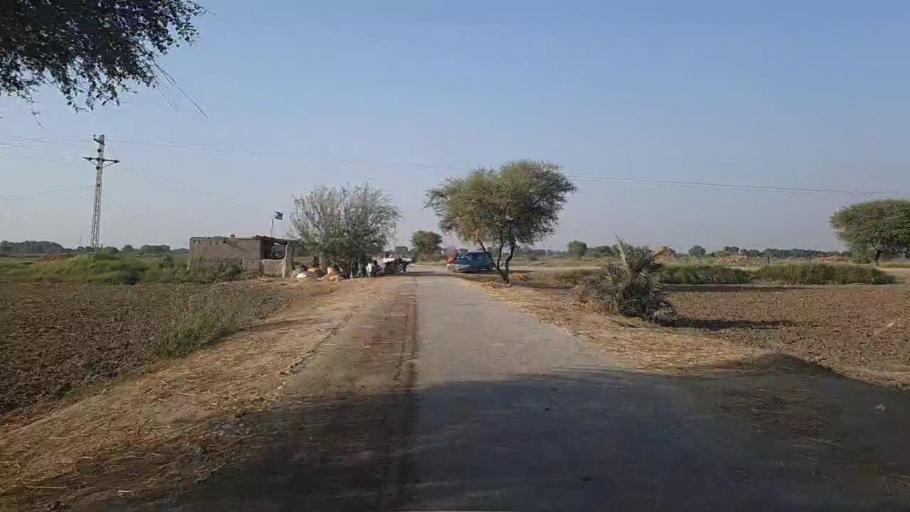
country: PK
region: Sindh
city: Kashmor
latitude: 28.4171
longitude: 69.4101
